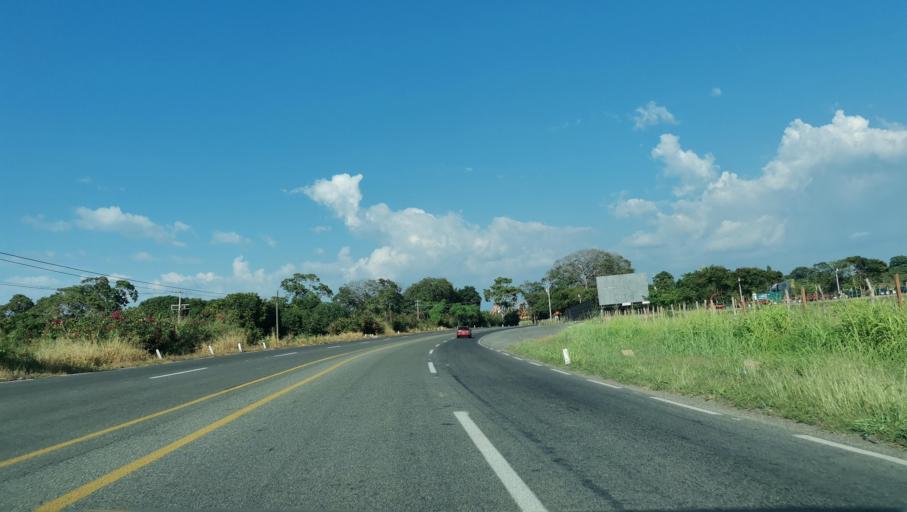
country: MX
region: Chiapas
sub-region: Tapachula
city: Congregacion Reforma
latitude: 14.8157
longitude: -92.3440
